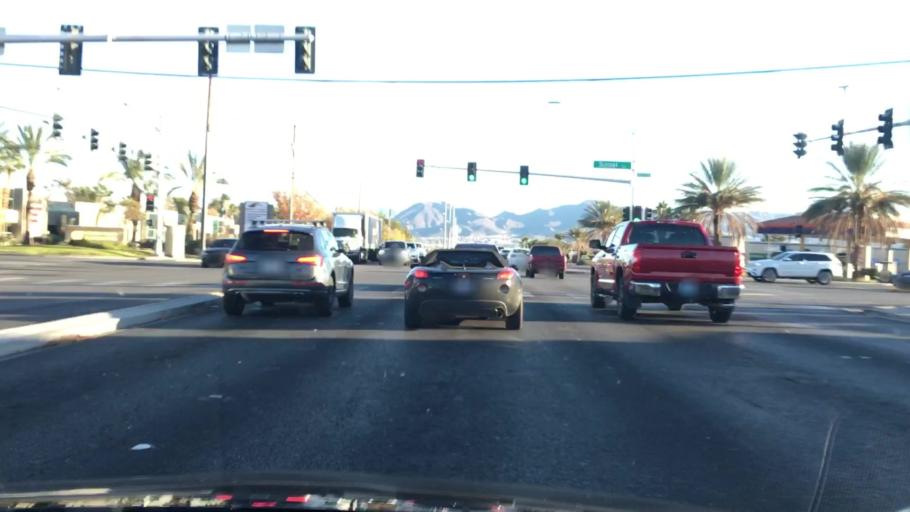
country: US
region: Nevada
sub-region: Clark County
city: Whitney
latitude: 36.0716
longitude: -115.0716
